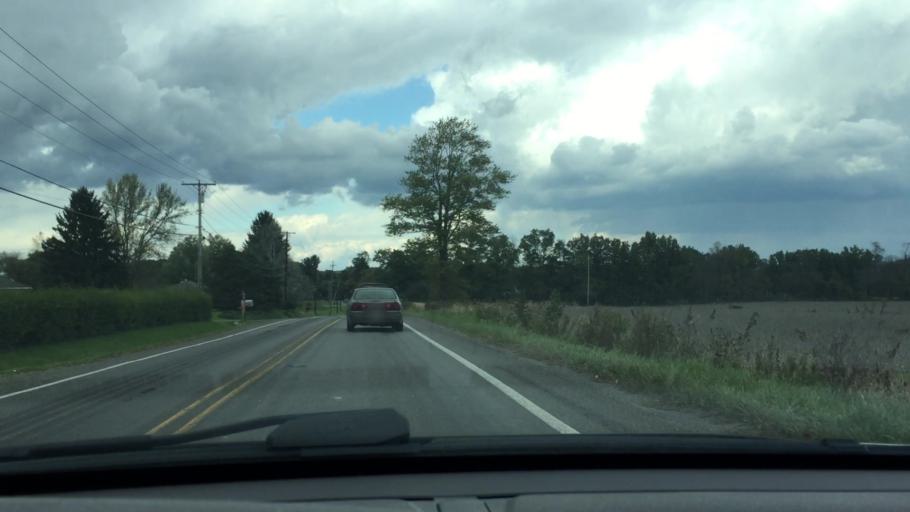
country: US
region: Pennsylvania
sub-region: Lawrence County
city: Oakwood
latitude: 40.9986
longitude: -80.4373
